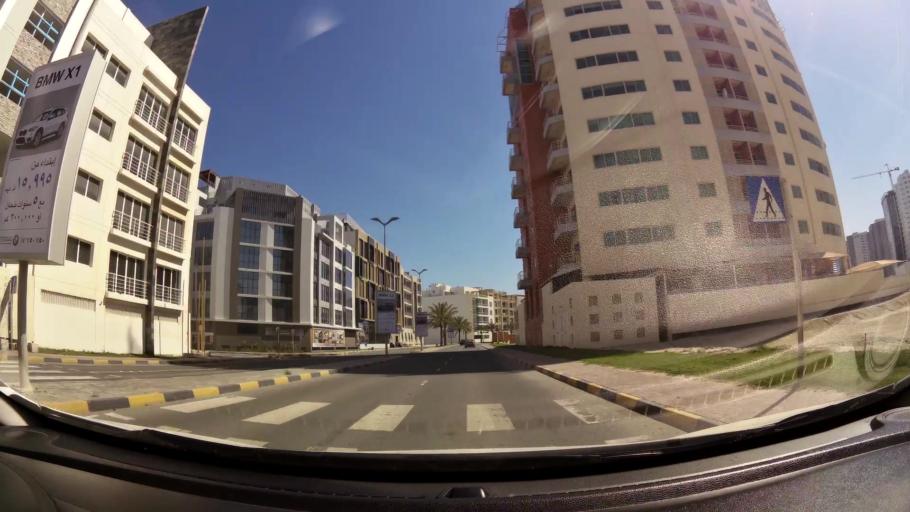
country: BH
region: Muharraq
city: Al Hadd
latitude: 26.2910
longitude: 50.6677
